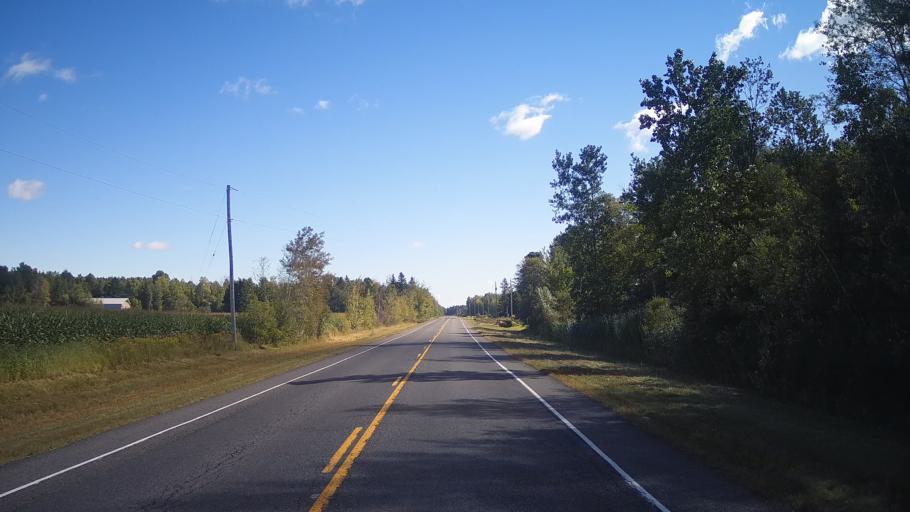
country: CA
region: Ontario
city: Prescott
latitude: 44.9115
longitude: -75.4259
